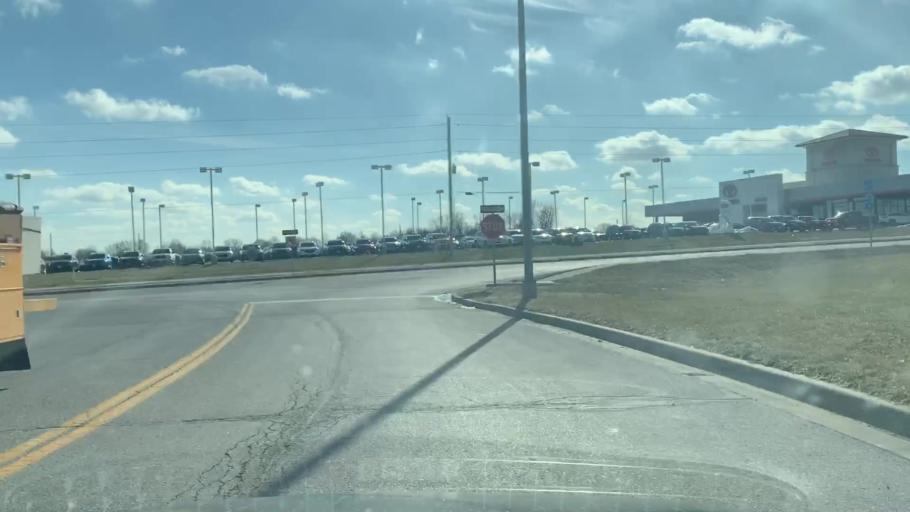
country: US
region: Missouri
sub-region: Jackson County
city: Lees Summit
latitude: 38.9467
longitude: -94.3668
